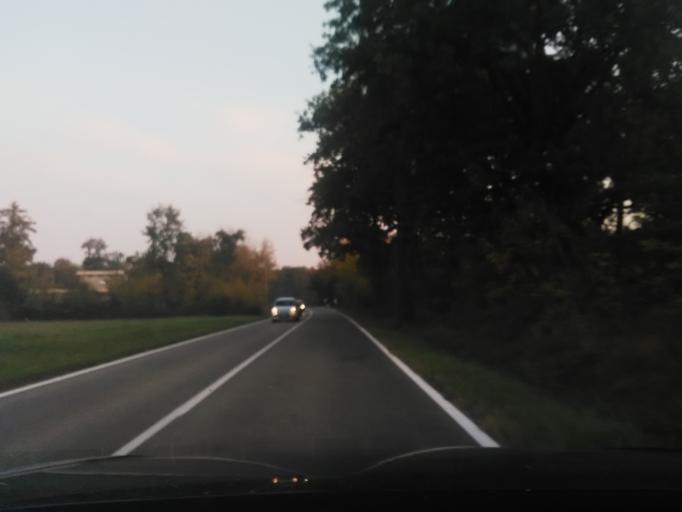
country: IT
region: Piedmont
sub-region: Provincia di Vercelli
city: San Maurizio
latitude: 45.5793
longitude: 8.2945
